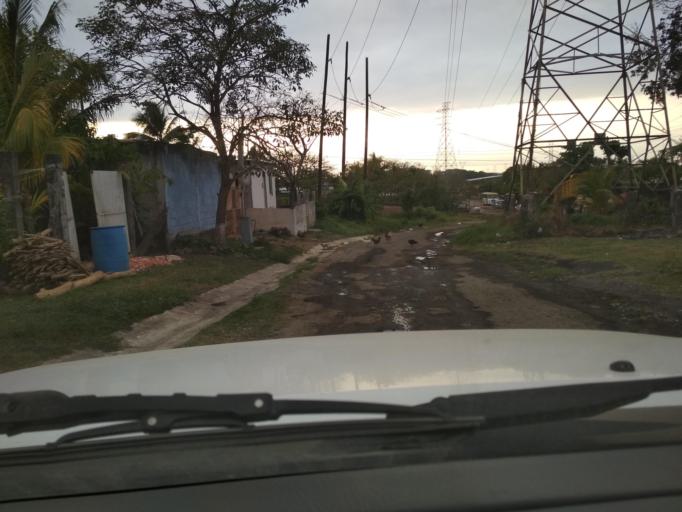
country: MX
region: Veracruz
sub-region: Medellin
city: Fraccionamiento Arboledas San Ramon
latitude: 19.0839
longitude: -96.1537
